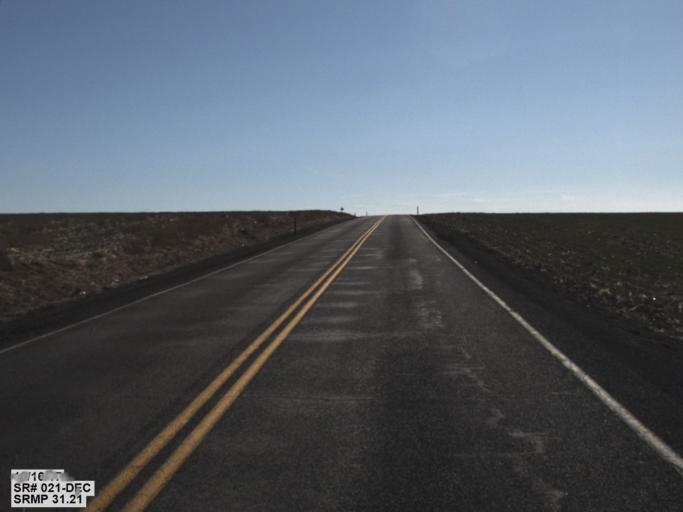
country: US
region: Washington
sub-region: Adams County
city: Ritzville
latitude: 47.0023
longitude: -118.6637
